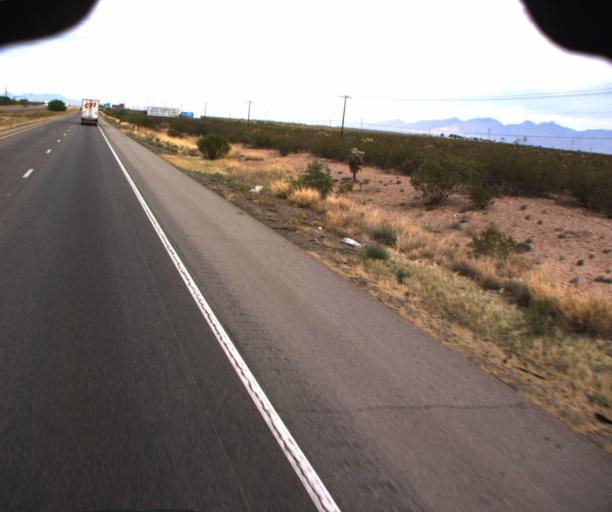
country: US
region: Arizona
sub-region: Pima County
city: Vail
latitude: 32.0520
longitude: -110.7582
